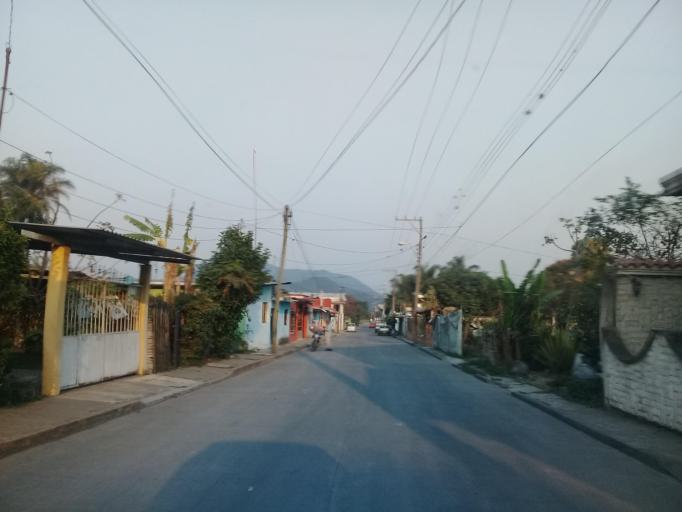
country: MX
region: Veracruz
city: Ixtac Zoquitlan
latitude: 18.8507
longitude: -97.0580
